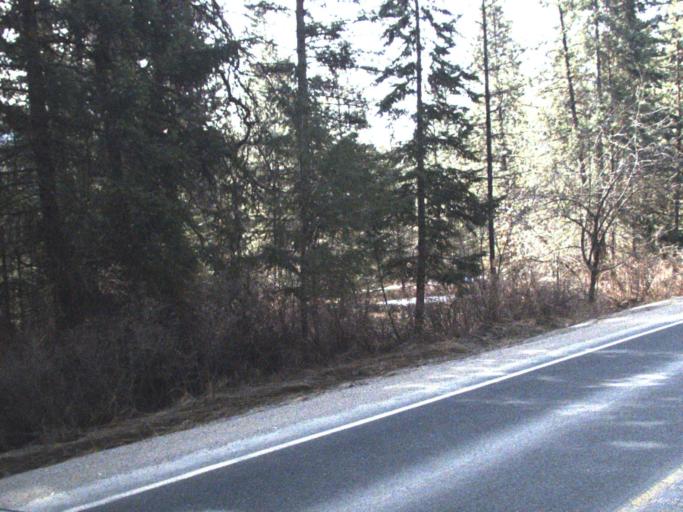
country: US
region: Washington
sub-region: Stevens County
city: Chewelah
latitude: 48.5111
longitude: -117.6620
